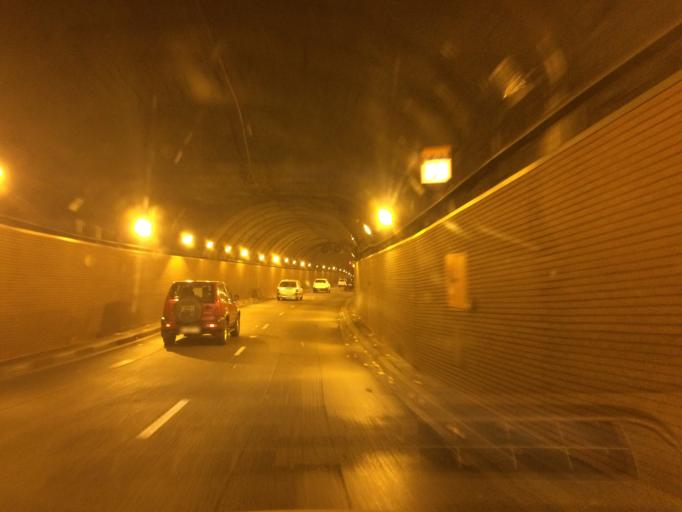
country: ES
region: Madrid
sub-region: Provincia de Madrid
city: Tetuan de las Victorias
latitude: 40.4605
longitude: -3.6978
